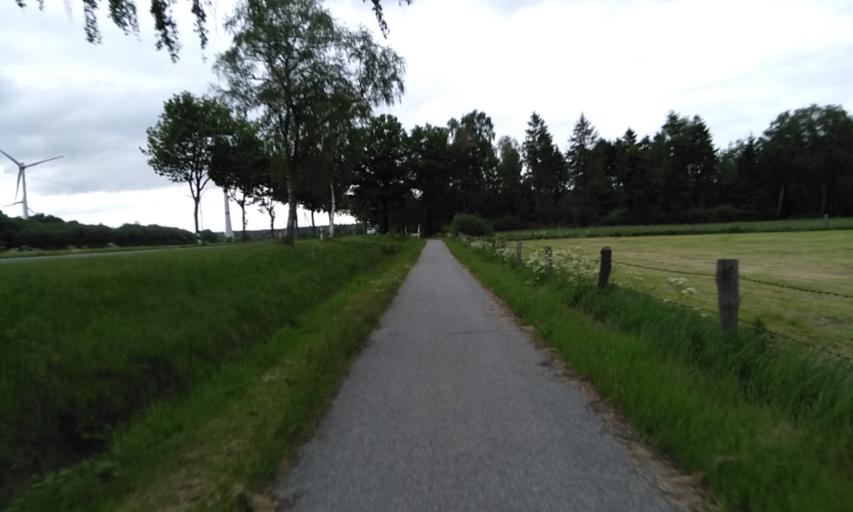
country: DE
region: Lower Saxony
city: Harsefeld
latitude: 53.4849
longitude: 9.4925
